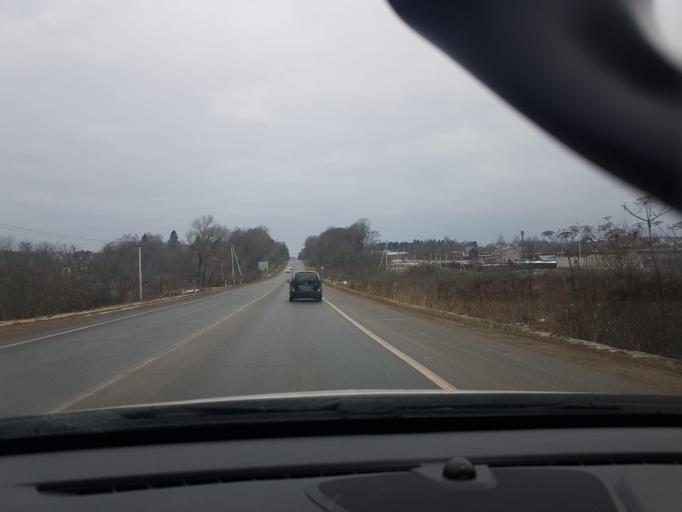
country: RU
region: Moskovskaya
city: Sychevo
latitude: 56.0075
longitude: 36.2362
